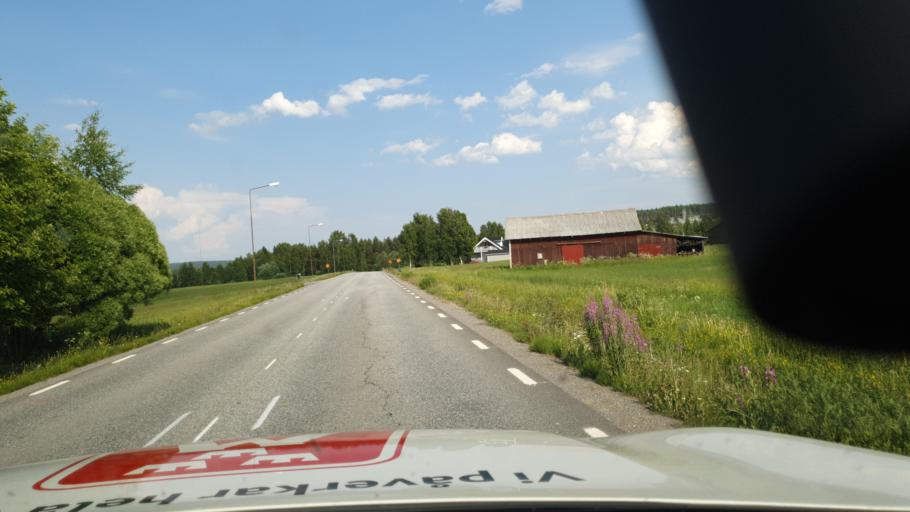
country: SE
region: Vaesterbotten
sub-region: Skelleftea Kommun
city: Viken
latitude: 64.7453
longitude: 20.8421
